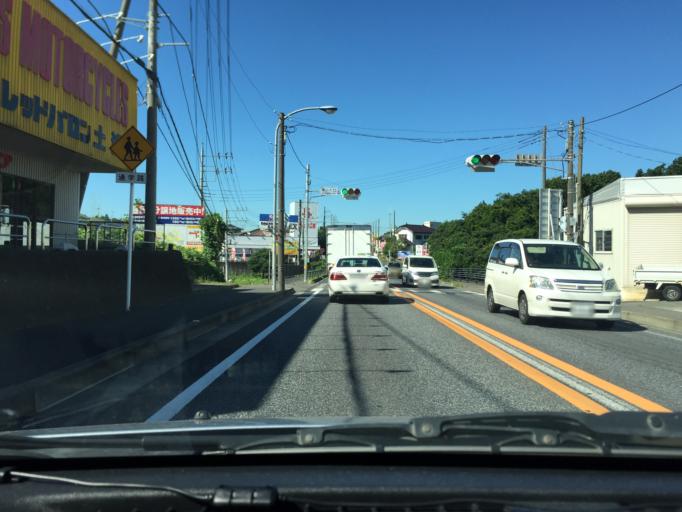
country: JP
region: Ibaraki
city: Naka
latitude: 36.0522
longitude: 140.1728
